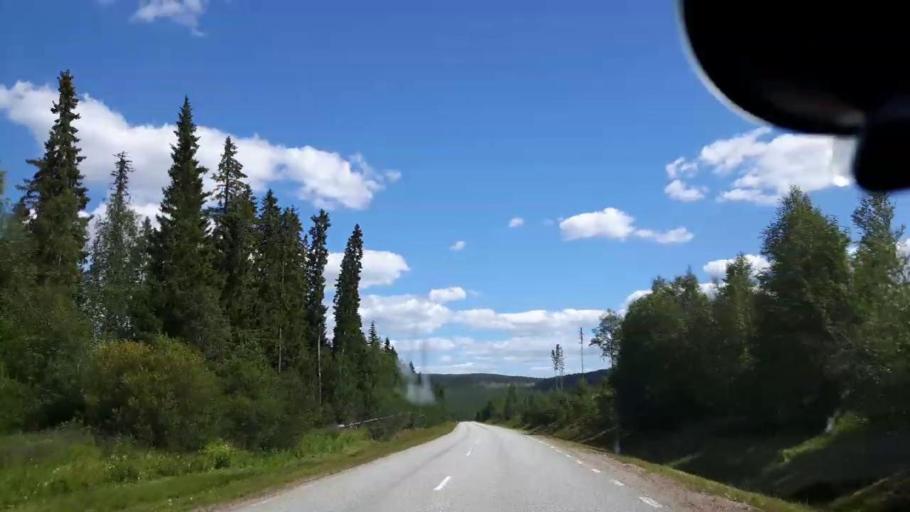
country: SE
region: Jaemtland
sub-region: Ragunda Kommun
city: Hammarstrand
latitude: 62.9595
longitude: 16.1846
